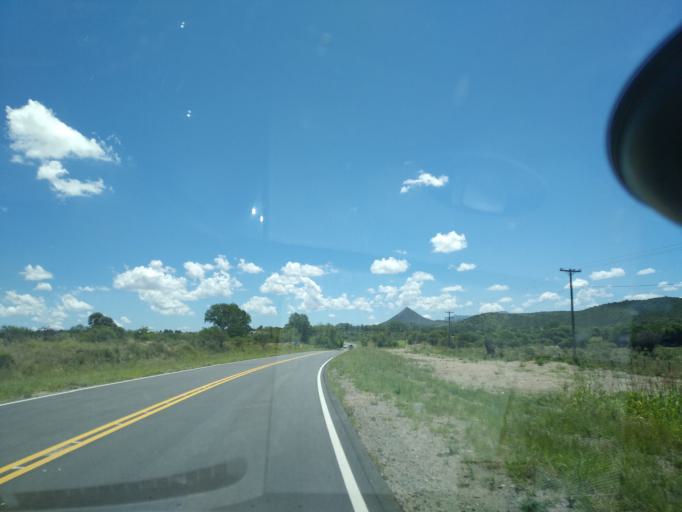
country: AR
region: Cordoba
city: Salsacate
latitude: -31.3505
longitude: -65.0884
